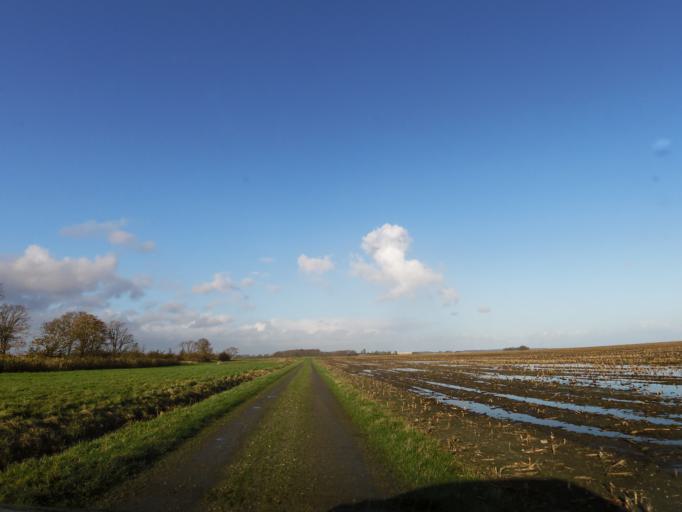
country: DK
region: Central Jutland
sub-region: Odder Kommune
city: Odder
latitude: 55.8439
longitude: 10.1923
